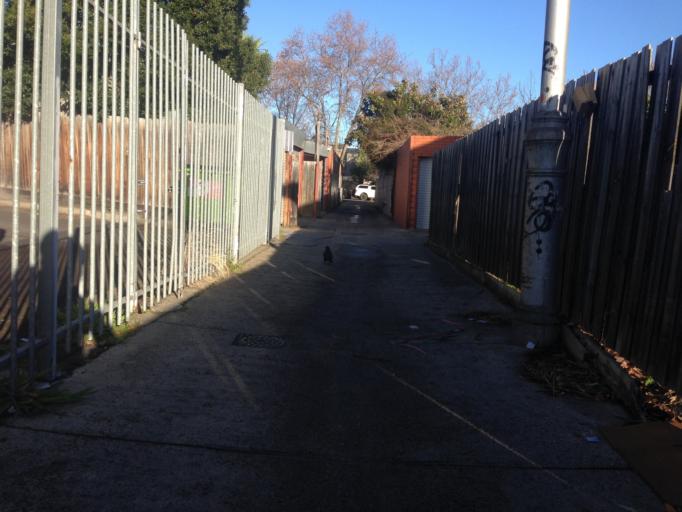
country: AU
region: Victoria
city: Alphington
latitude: -37.7802
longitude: 145.0320
